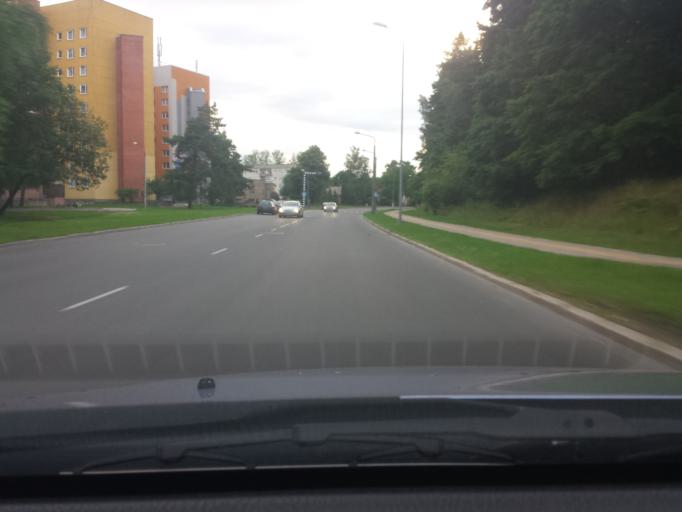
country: LV
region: Stopini
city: Ulbroka
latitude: 56.9715
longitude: 24.2419
